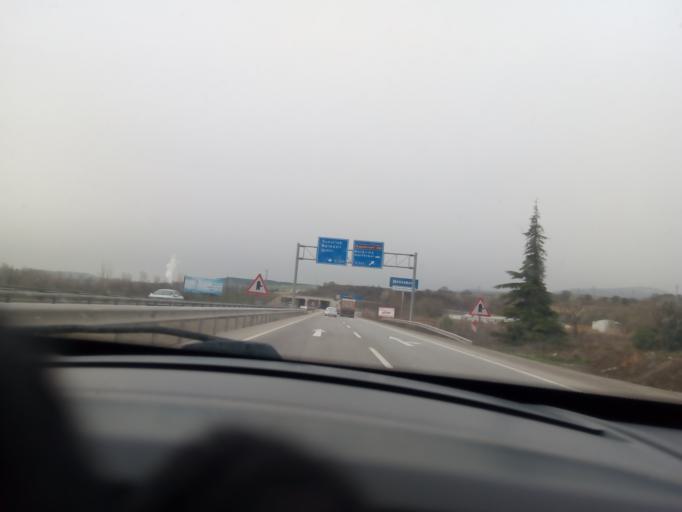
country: TR
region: Balikesir
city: Gobel
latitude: 39.9753
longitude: 28.1774
